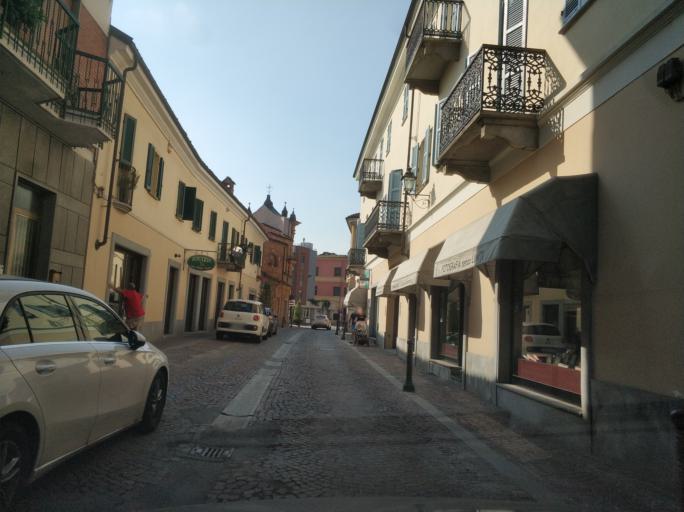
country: IT
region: Piedmont
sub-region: Provincia di Cuneo
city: Bra
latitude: 44.6997
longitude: 7.8493
